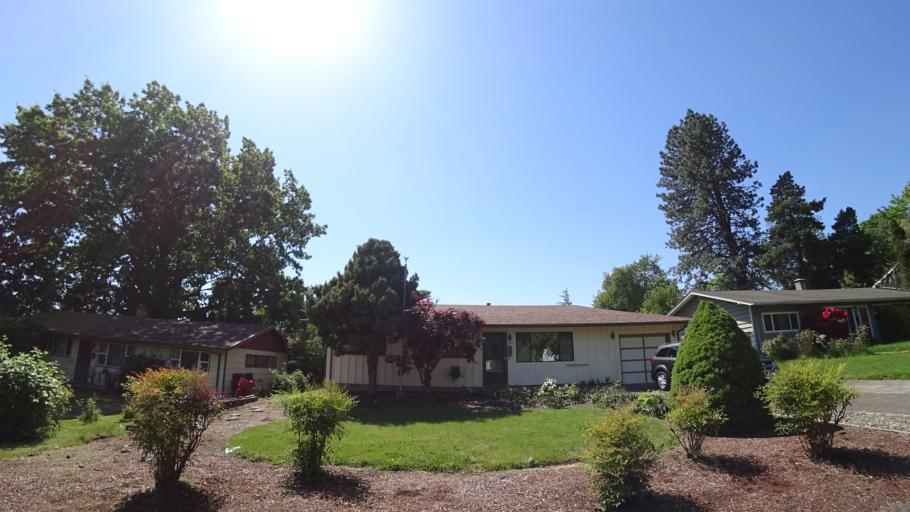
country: US
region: Oregon
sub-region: Washington County
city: Beaverton
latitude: 45.4952
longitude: -122.8011
